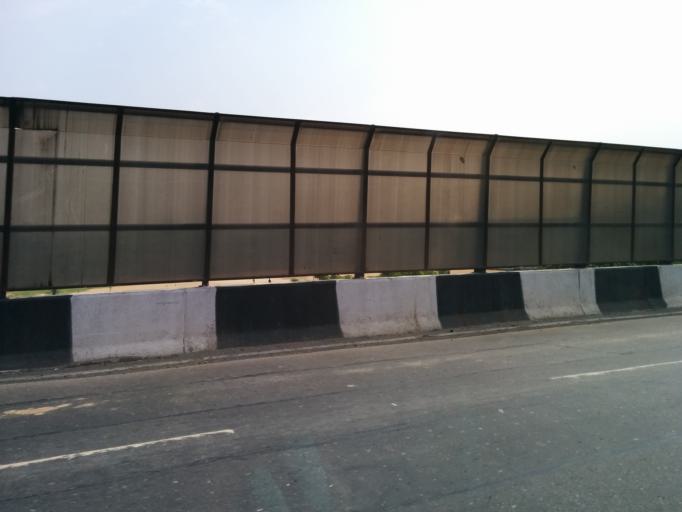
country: IN
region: NCT
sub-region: New Delhi
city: New Delhi
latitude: 28.5502
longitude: 77.1847
